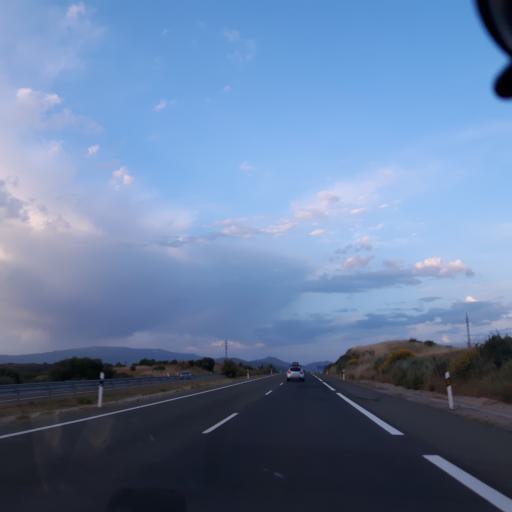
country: ES
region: Castille and Leon
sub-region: Provincia de Salamanca
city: Guijuelo
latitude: 40.5378
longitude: -5.6635
